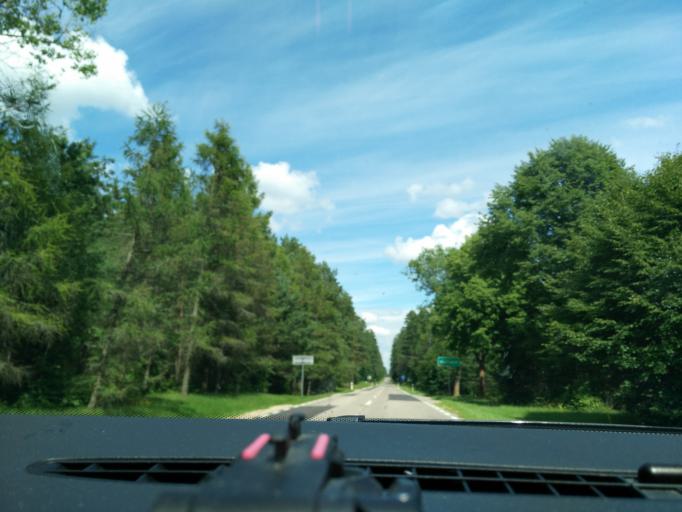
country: PL
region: Podlasie
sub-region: Powiat sejnenski
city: Krasnopol
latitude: 53.9586
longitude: 23.2231
